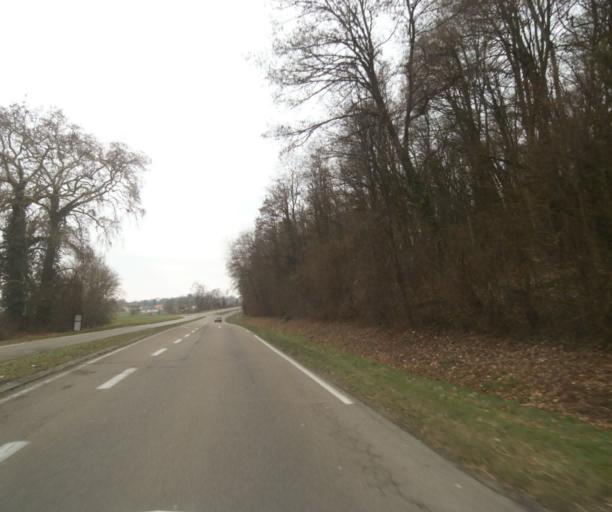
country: FR
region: Champagne-Ardenne
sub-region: Departement de la Haute-Marne
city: Bienville
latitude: 48.5935
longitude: 5.0309
